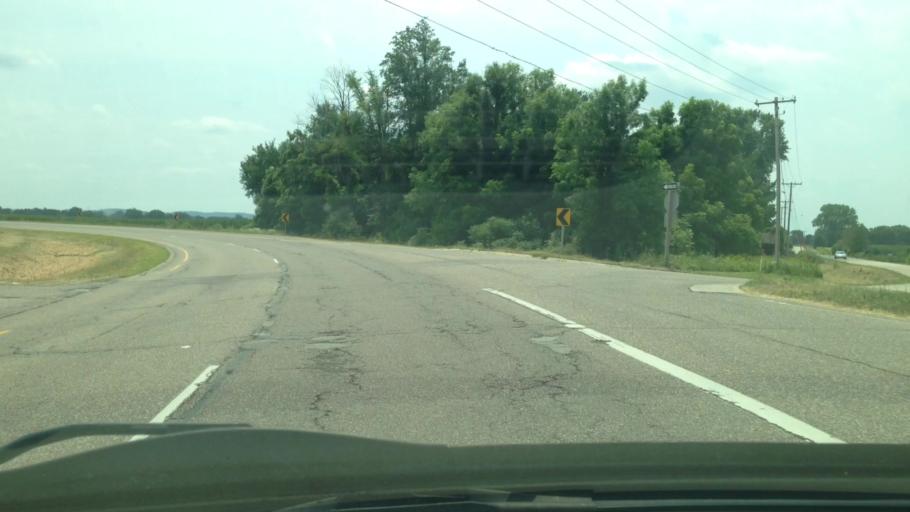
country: US
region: Wisconsin
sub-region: Sauk County
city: Prairie du Sac
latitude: 43.3520
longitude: -89.7677
